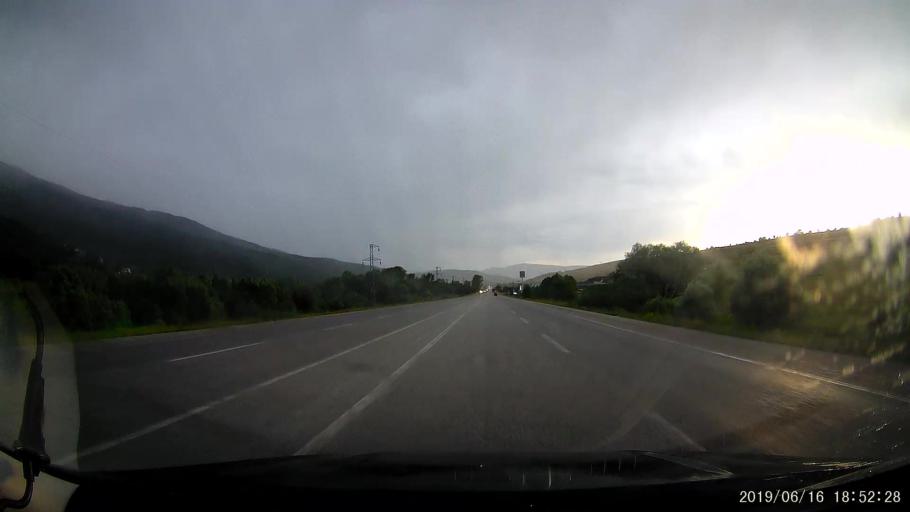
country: TR
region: Erzincan
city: Catalcam
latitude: 39.9025
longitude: 38.9009
